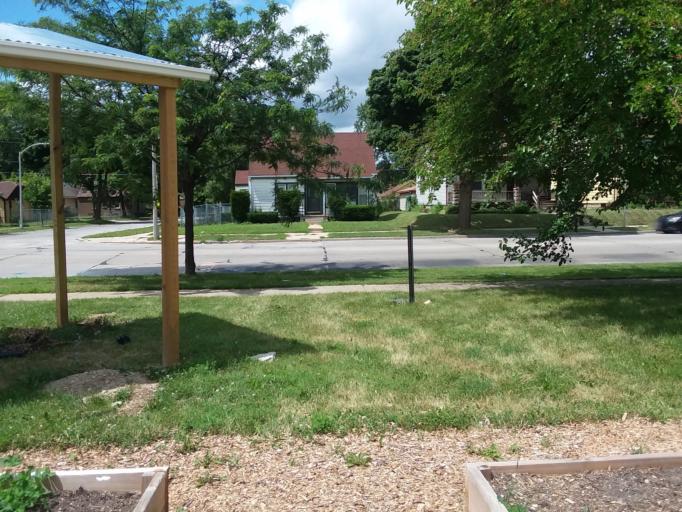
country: US
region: Wisconsin
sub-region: Milwaukee County
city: Glendale
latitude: 43.0991
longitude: -87.9465
